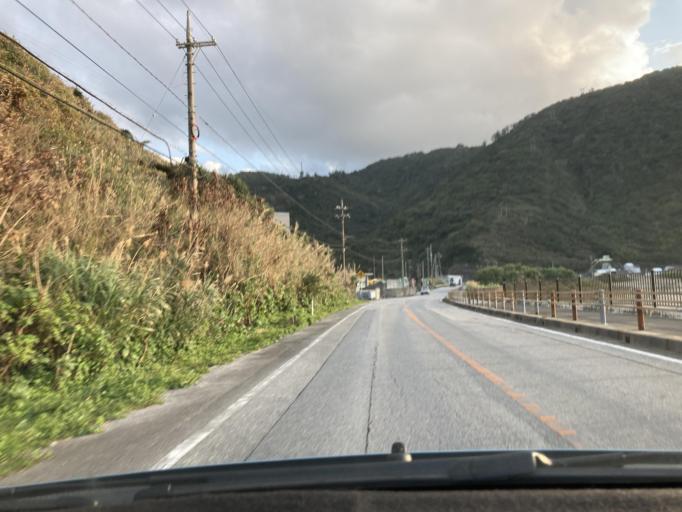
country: JP
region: Okinawa
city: Nago
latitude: 26.7998
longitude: 128.2325
